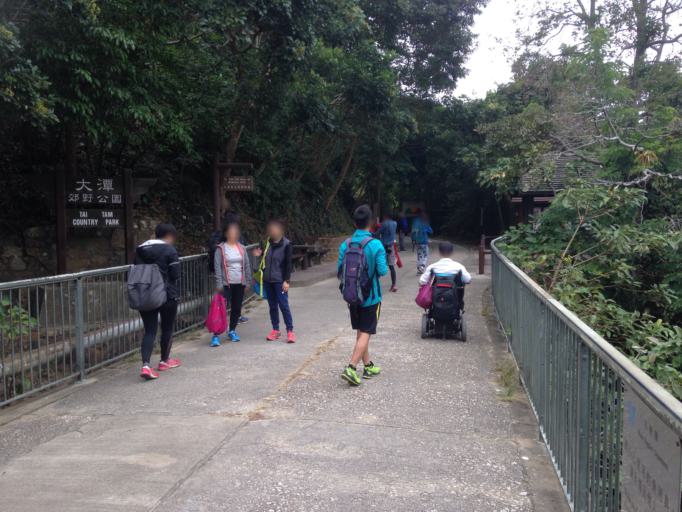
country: HK
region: Wanchai
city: Wan Chai
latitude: 22.2402
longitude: 114.2211
